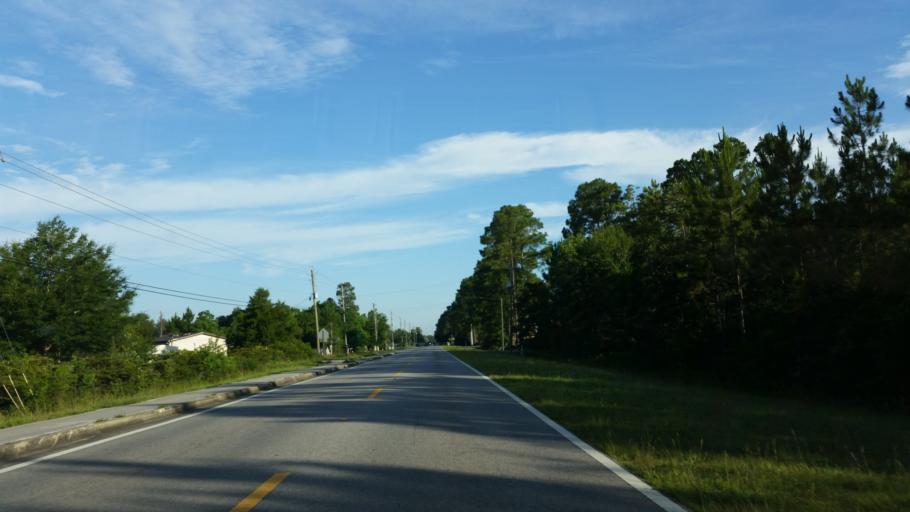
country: US
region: Florida
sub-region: Escambia County
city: Myrtle Grove
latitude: 30.3883
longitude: -87.3593
